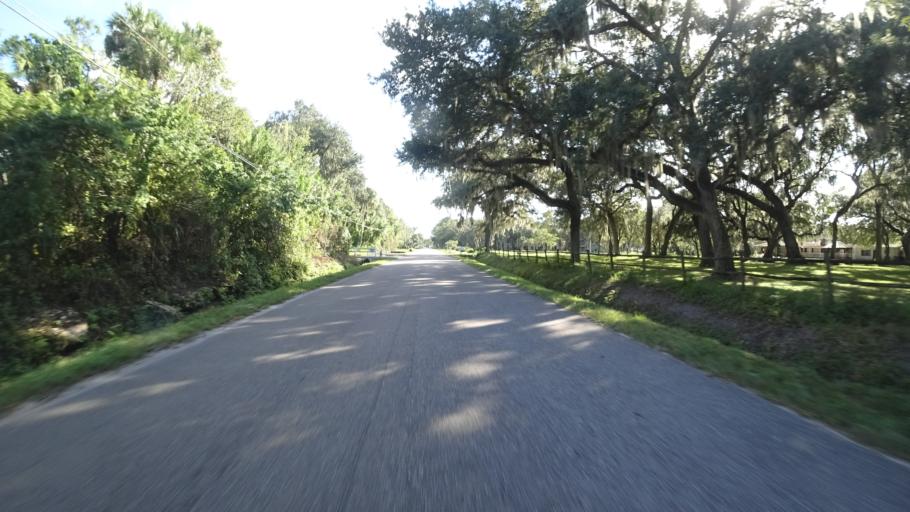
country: US
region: Florida
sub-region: Manatee County
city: Ellenton
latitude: 27.4812
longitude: -82.4795
